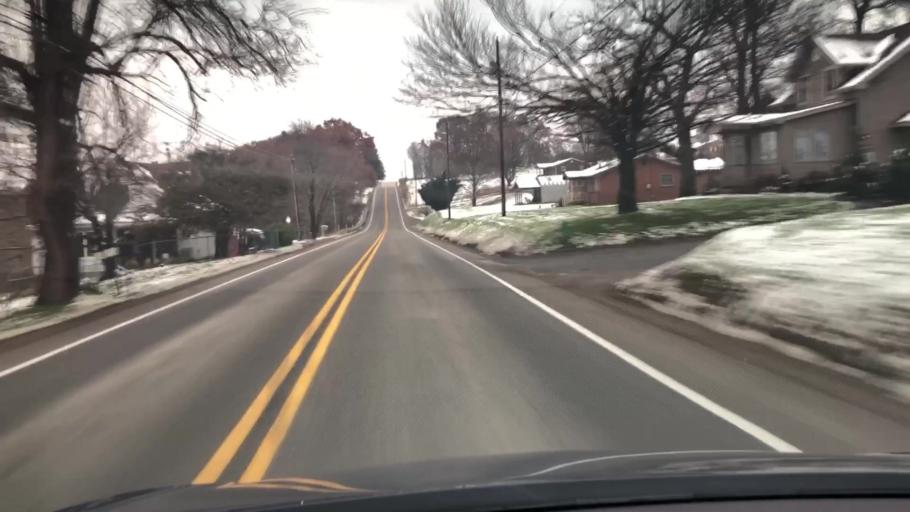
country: US
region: Pennsylvania
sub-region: Armstrong County
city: Kittanning
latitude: 40.8882
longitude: -79.3871
